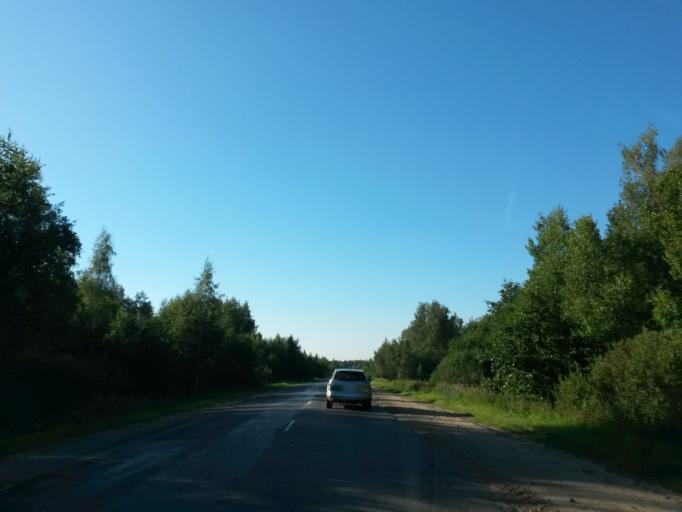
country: RU
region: Ivanovo
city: Novo-Talitsy
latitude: 57.0351
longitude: 40.7476
